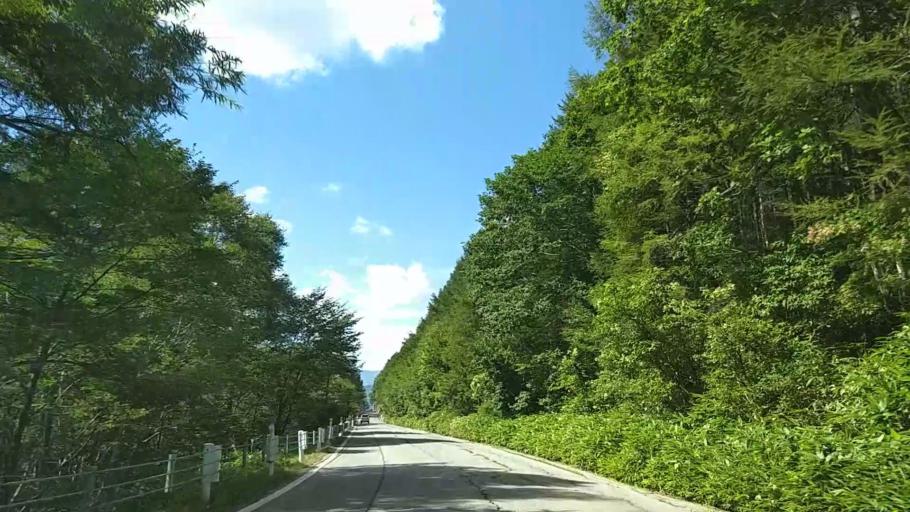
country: JP
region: Nagano
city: Chino
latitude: 36.0896
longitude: 138.2771
